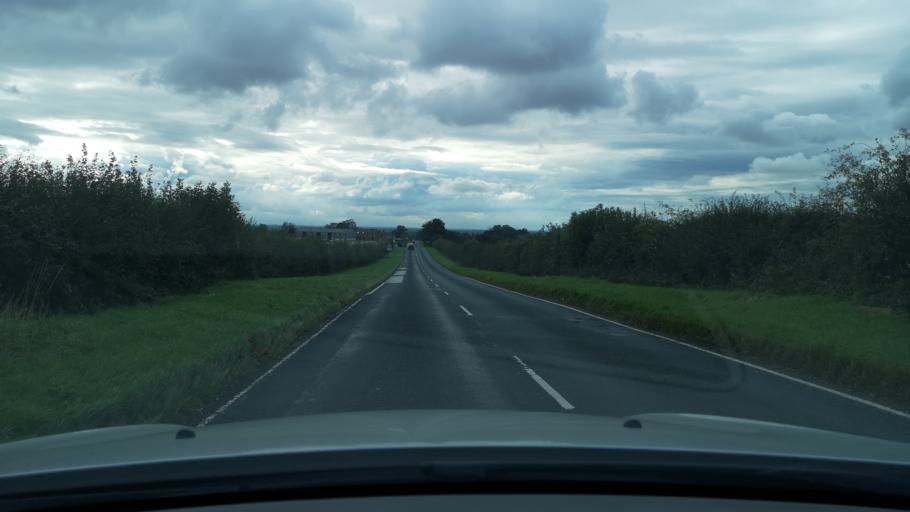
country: GB
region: England
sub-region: East Riding of Yorkshire
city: Hotham
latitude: 53.7905
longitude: -0.6172
